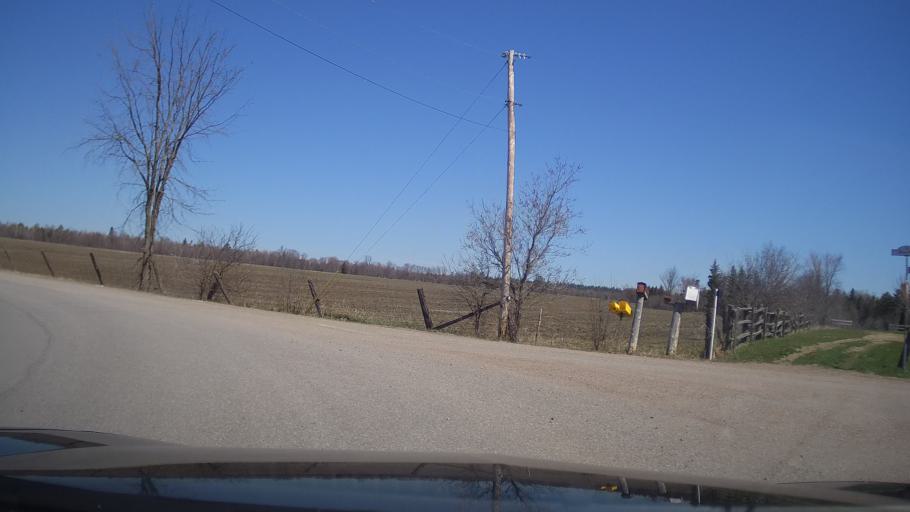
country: CA
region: Quebec
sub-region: Outaouais
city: Shawville
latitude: 45.5363
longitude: -76.3917
